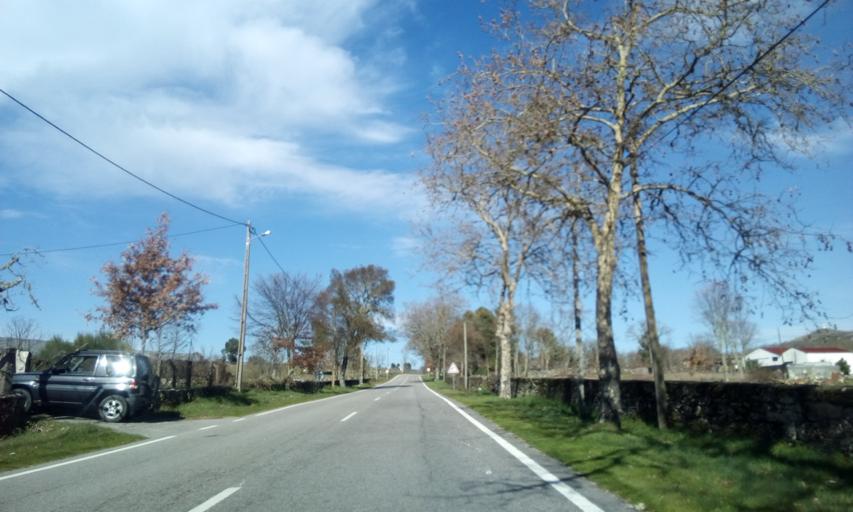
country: PT
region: Guarda
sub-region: Guarda
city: Sequeira
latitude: 40.5865
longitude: -7.1477
